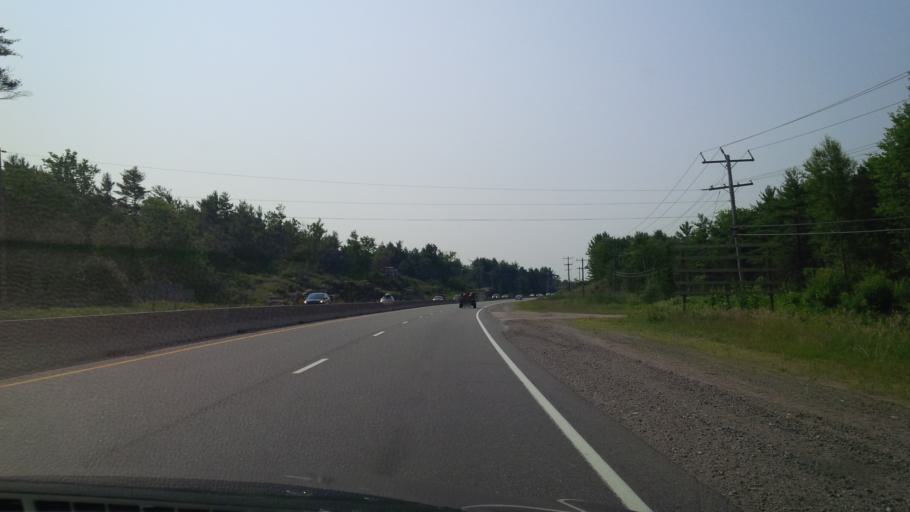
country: CA
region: Ontario
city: Gravenhurst
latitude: 44.8732
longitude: -79.3287
